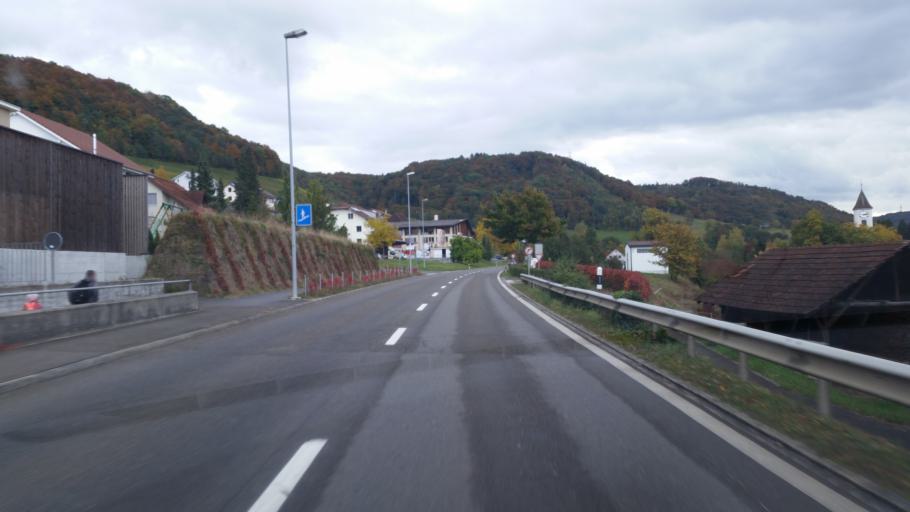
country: CH
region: Aargau
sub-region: Bezirk Zurzach
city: Tegerfelden
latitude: 47.5596
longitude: 8.2891
